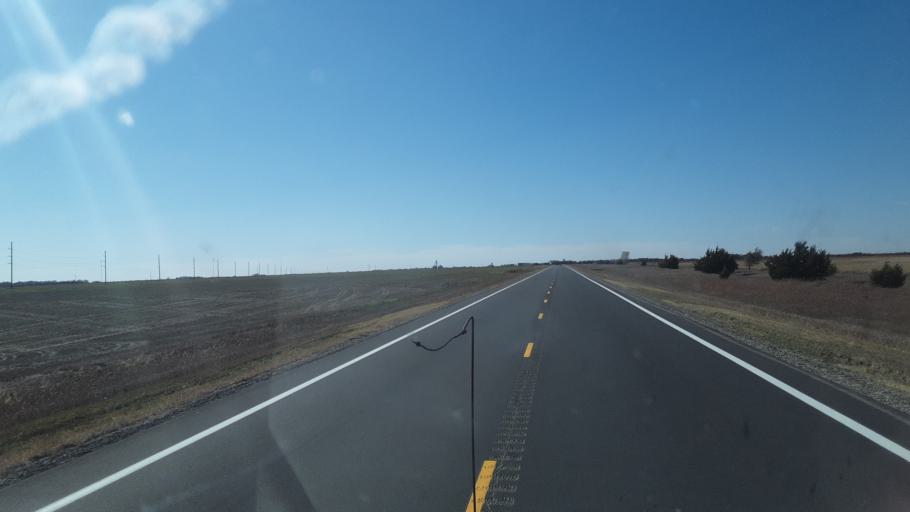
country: US
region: Kansas
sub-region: Rice County
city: Lyons
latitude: 38.3677
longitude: -98.1516
